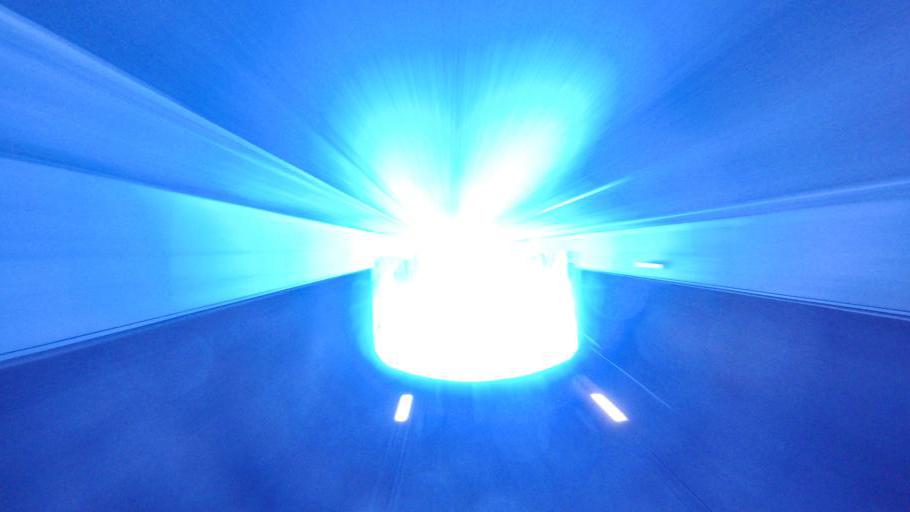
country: FI
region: Uusimaa
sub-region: Helsinki
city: Saukkola
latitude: 60.3356
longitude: 23.9293
